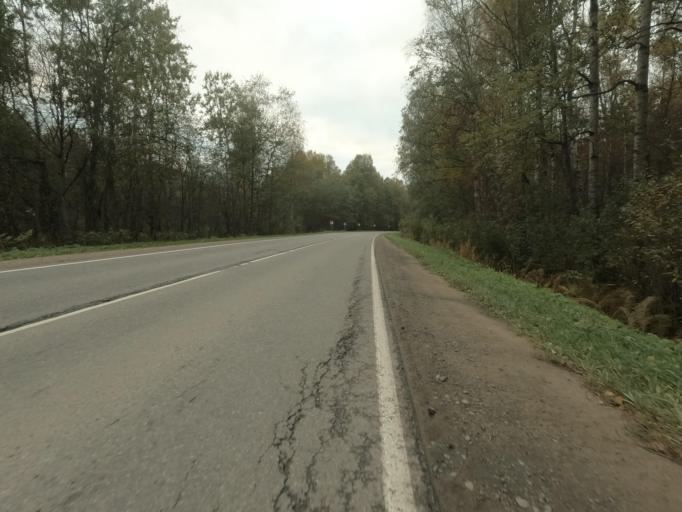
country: RU
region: Leningrad
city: Pavlovo
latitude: 59.7968
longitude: 30.9468
